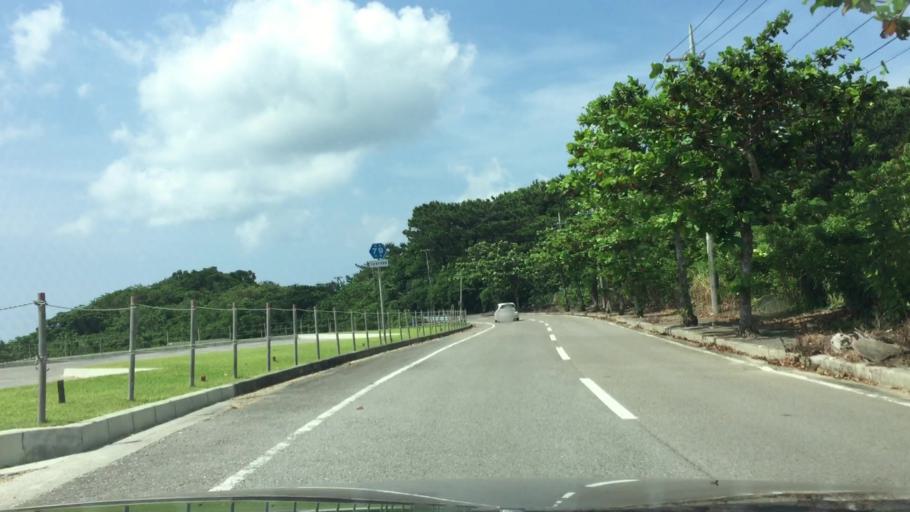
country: JP
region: Okinawa
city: Ishigaki
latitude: 24.4708
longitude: 124.2244
